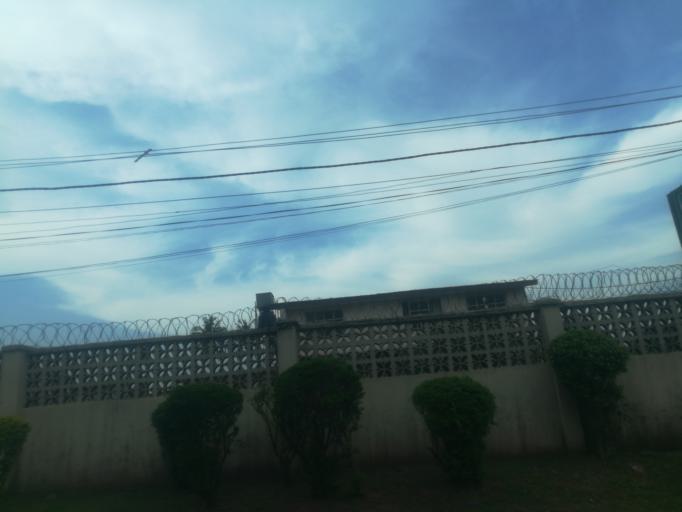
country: NG
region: Oyo
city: Ibadan
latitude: 7.4235
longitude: 3.9082
